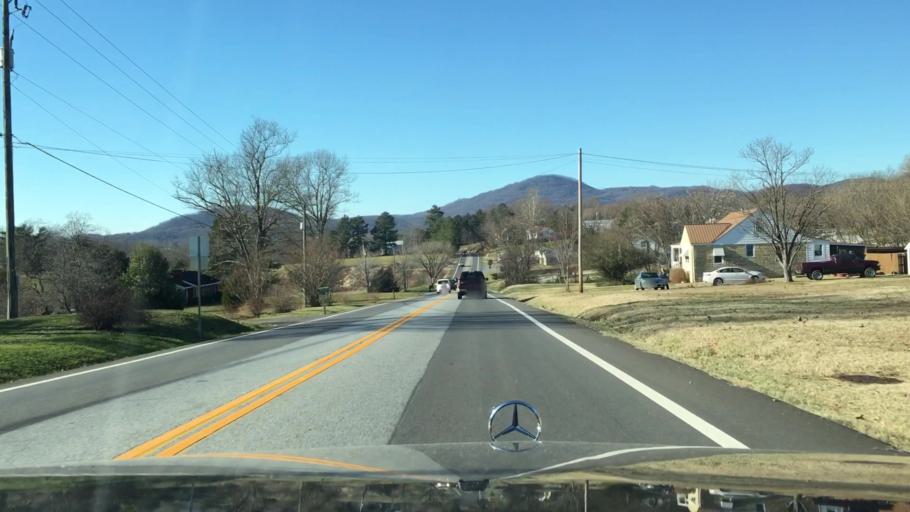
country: US
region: Virginia
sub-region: Botetourt County
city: Blue Ridge
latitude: 37.2690
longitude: -79.7622
